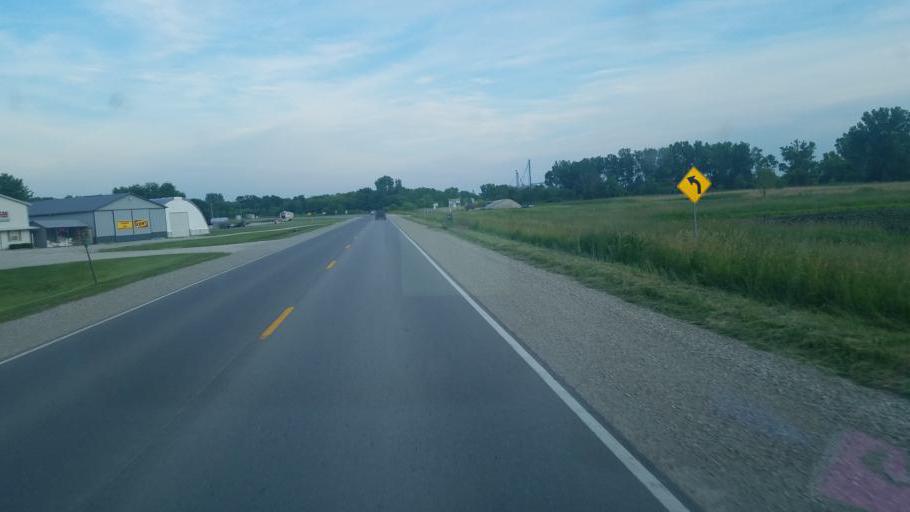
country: US
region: Iowa
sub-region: Benton County
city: Belle Plaine
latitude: 41.9006
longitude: -92.2920
